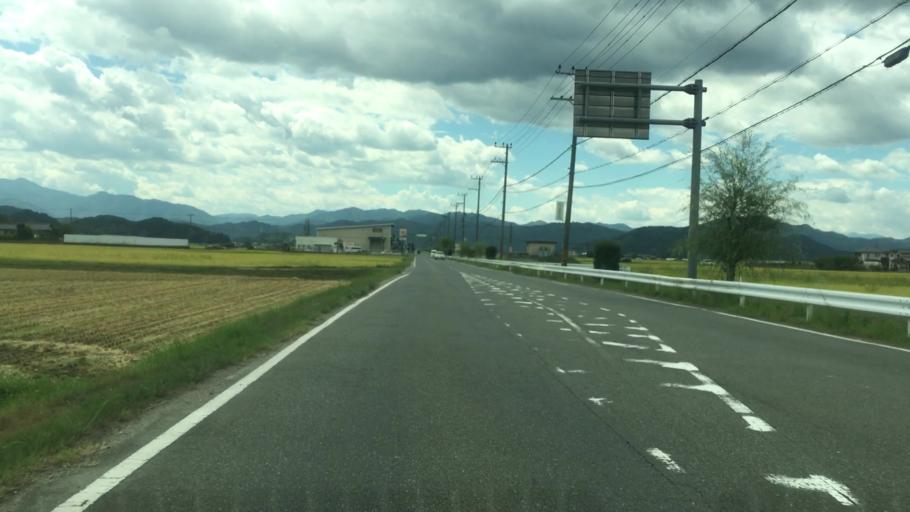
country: JP
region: Hyogo
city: Toyooka
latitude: 35.5273
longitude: 134.8398
